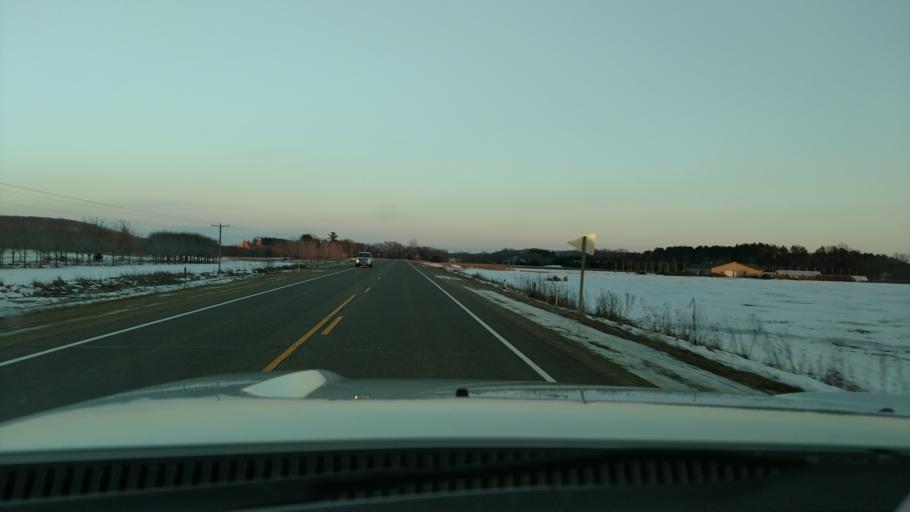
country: US
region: Wisconsin
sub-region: Pierce County
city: River Falls
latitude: 44.8982
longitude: -92.5965
